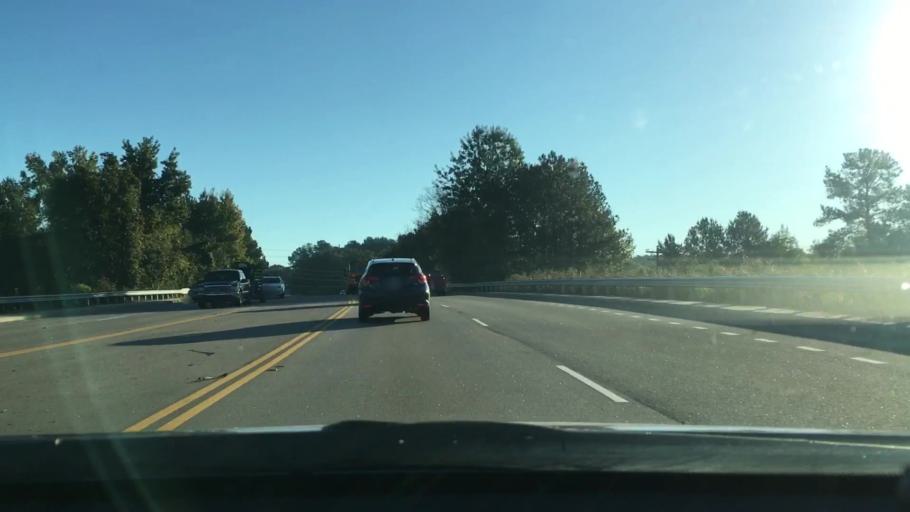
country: US
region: South Carolina
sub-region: Lexington County
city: West Columbia
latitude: 34.0266
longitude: -81.0652
